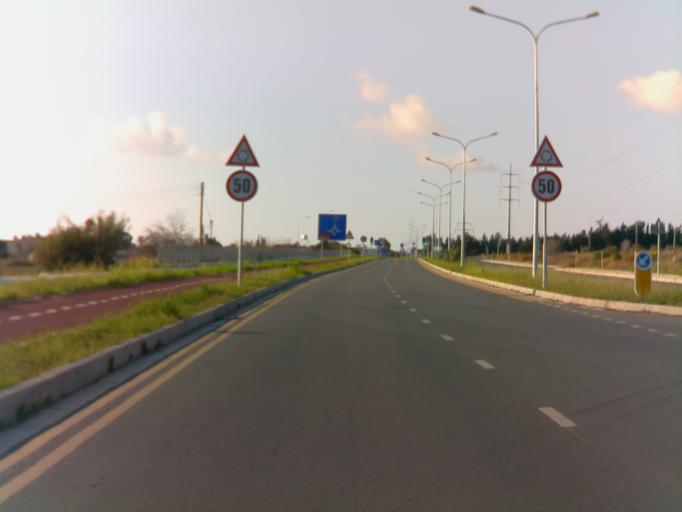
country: CY
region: Pafos
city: Paphos
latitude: 34.7472
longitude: 32.4368
